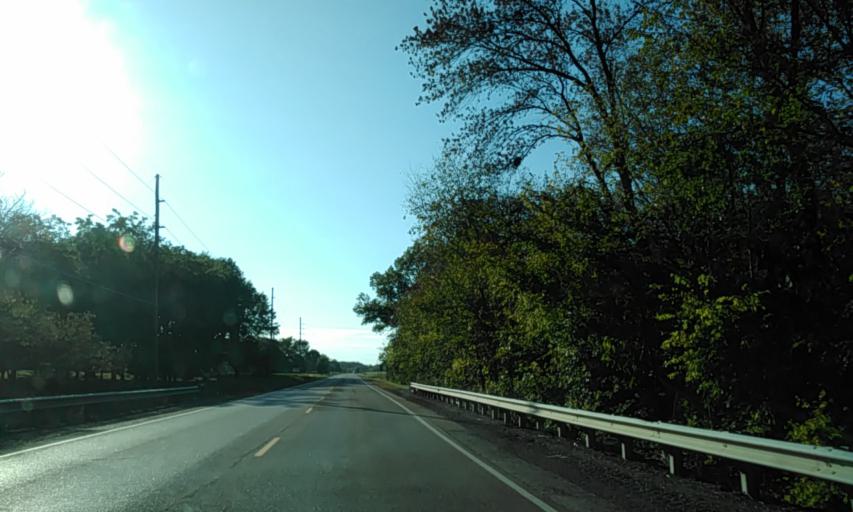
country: US
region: Illinois
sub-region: Madison County
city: Saint Jacob
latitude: 38.7161
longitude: -89.8117
